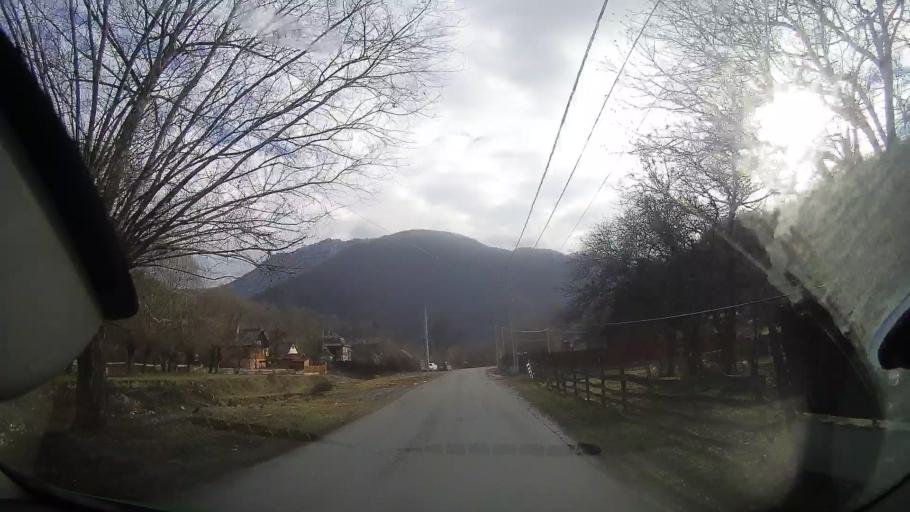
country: RO
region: Alba
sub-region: Comuna Ocolis
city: Ocolis
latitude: 46.4737
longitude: 23.4713
